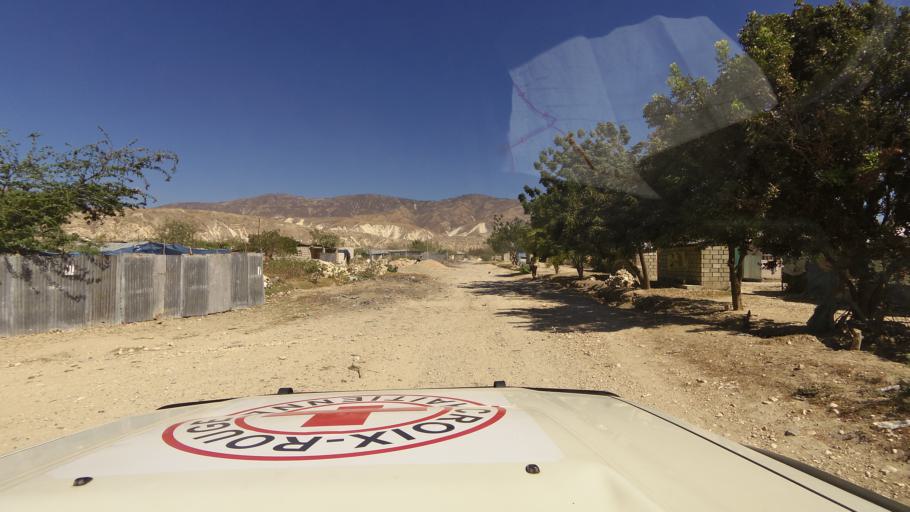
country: HT
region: Ouest
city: Croix des Bouquets
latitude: 18.6539
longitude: -72.2541
